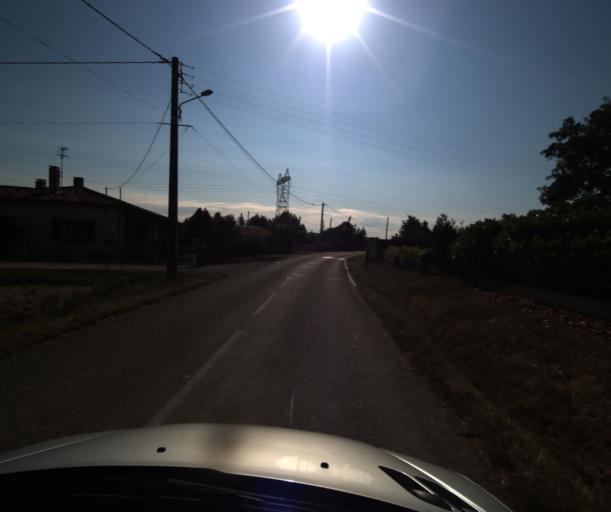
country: FR
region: Midi-Pyrenees
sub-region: Departement du Tarn-et-Garonne
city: Bressols
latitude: 43.9687
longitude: 1.3193
